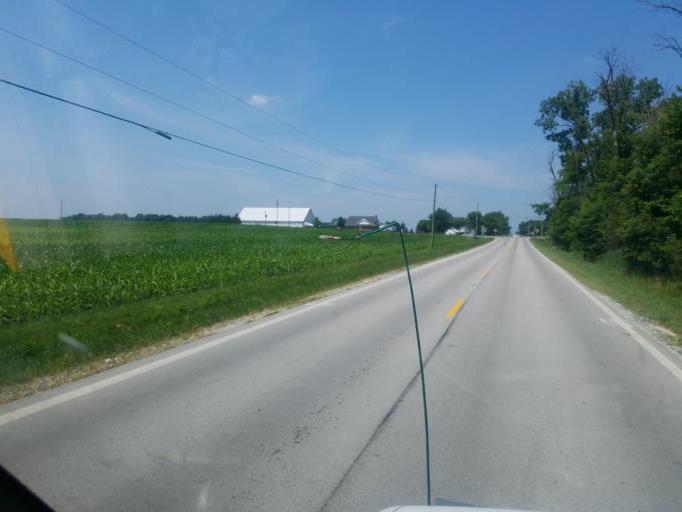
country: US
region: Ohio
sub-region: Auglaize County
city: Minster
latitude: 40.4061
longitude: -84.4338
